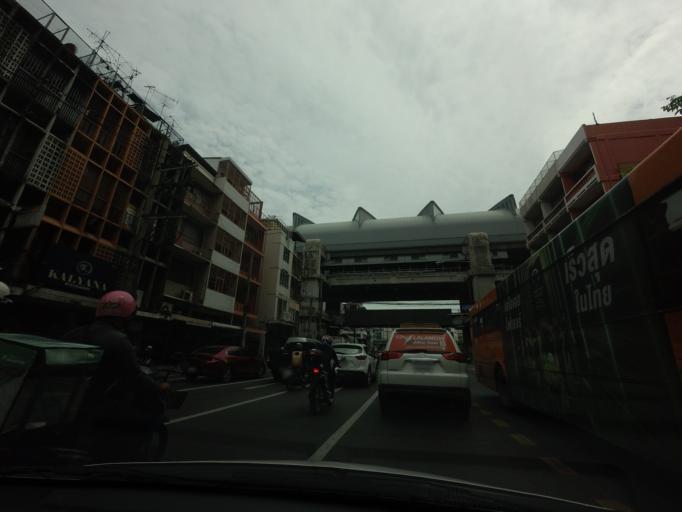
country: TH
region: Bangkok
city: Ratchathewi
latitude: 13.7554
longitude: 100.5417
